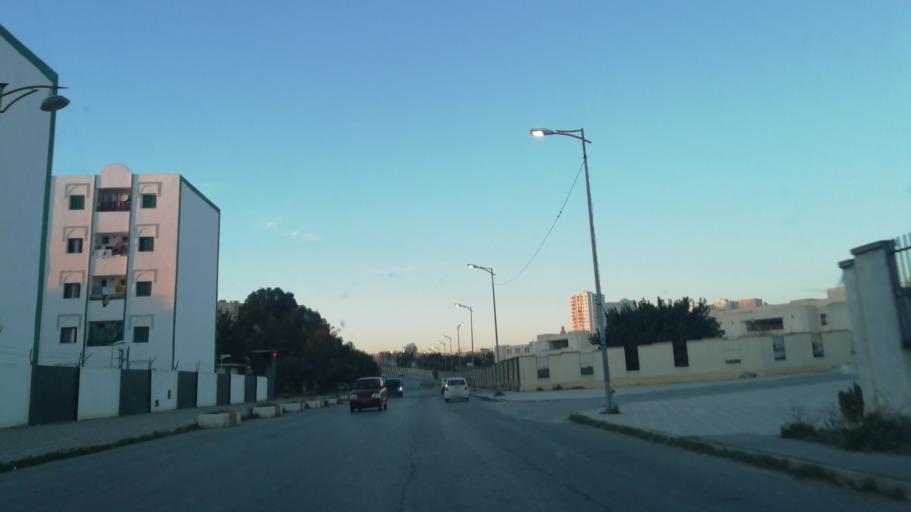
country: DZ
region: Oran
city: Bir el Djir
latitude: 35.7051
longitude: -0.5853
